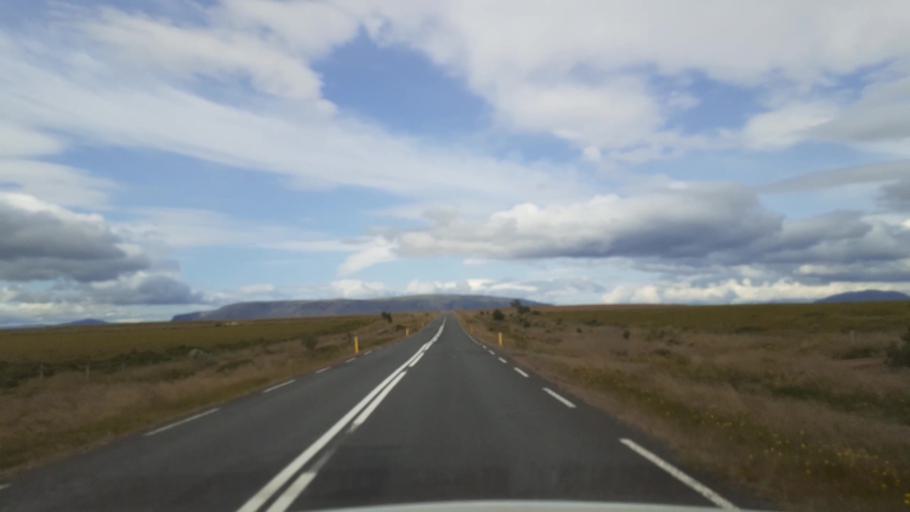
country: IS
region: South
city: Selfoss
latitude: 63.9146
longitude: -20.8368
